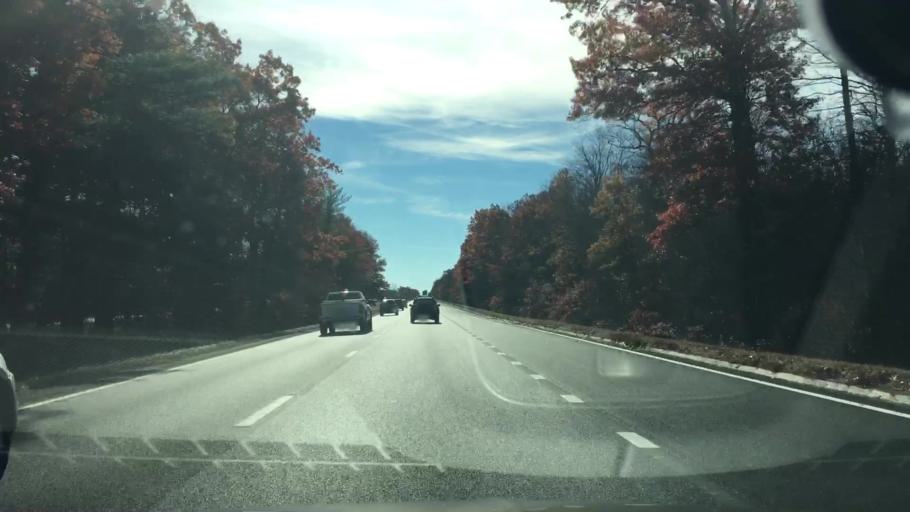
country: US
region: Massachusetts
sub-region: Franklin County
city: Whately
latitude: 42.4558
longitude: -72.6180
